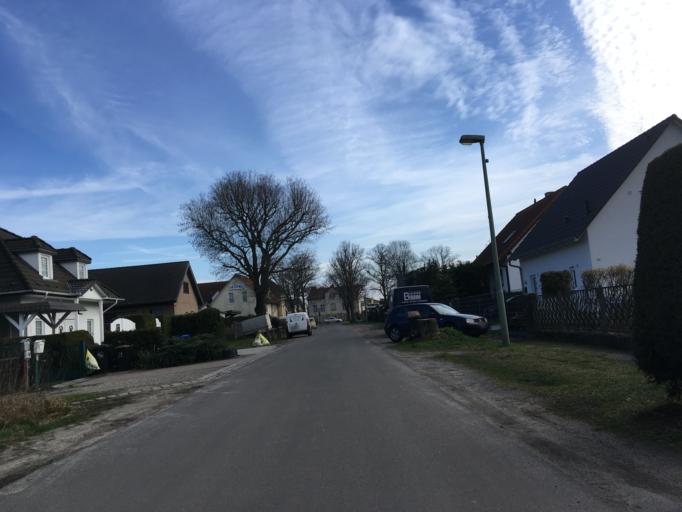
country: DE
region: Berlin
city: Buchholz
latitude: 52.6154
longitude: 13.4402
